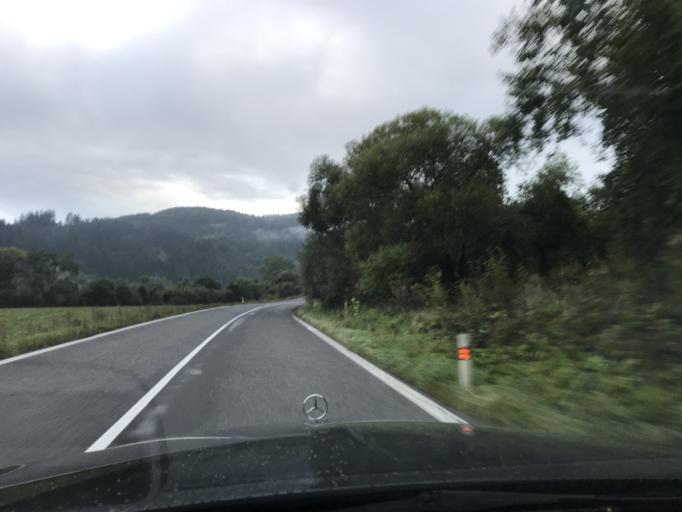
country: SK
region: Zilinsky
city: Tvrdosin
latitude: 49.3011
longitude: 19.4828
